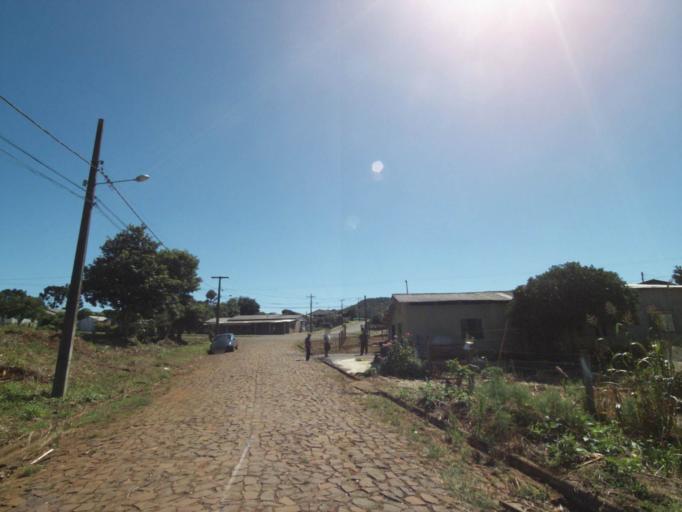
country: BR
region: Santa Catarina
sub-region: Sao Lourenco Do Oeste
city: Sao Lourenco dOeste
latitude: -26.2723
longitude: -52.7812
